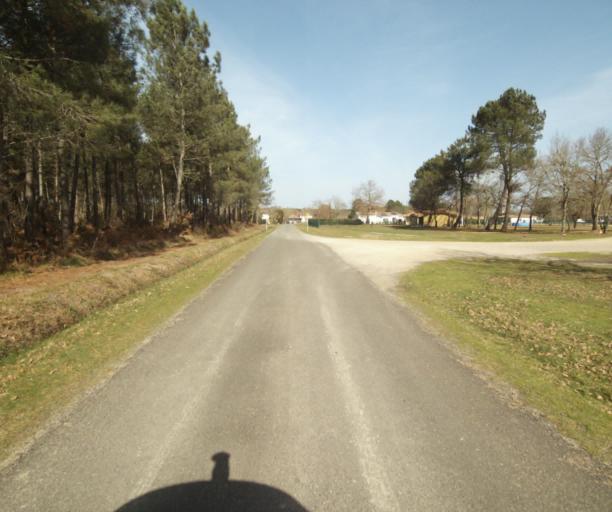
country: FR
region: Aquitaine
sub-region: Departement de la Gironde
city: Bazas
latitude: 44.2444
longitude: -0.1984
